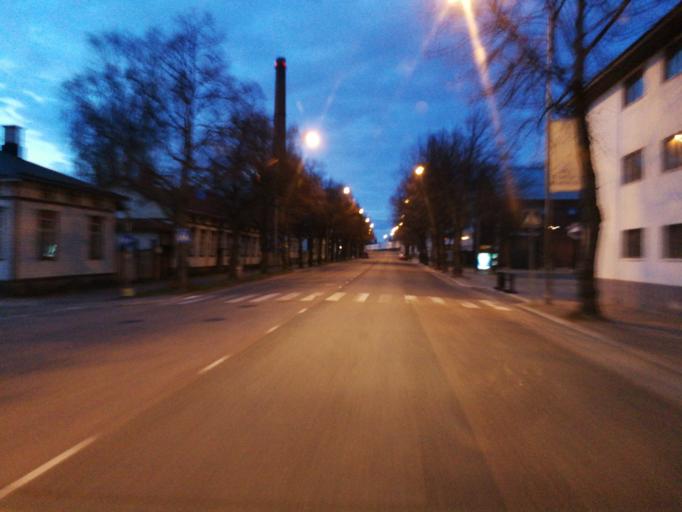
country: FI
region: Varsinais-Suomi
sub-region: Turku
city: Turku
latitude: 60.4369
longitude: 22.2343
